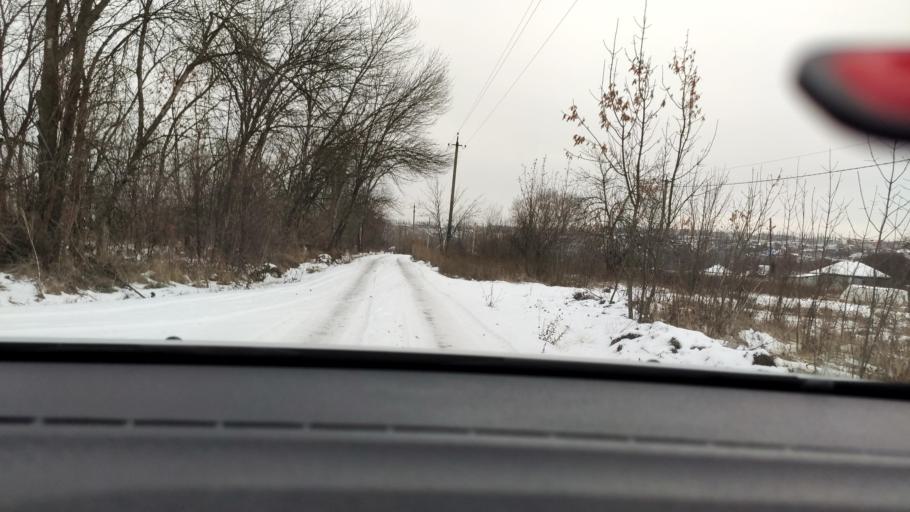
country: RU
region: Voronezj
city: Semiluki
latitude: 51.7028
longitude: 38.9897
